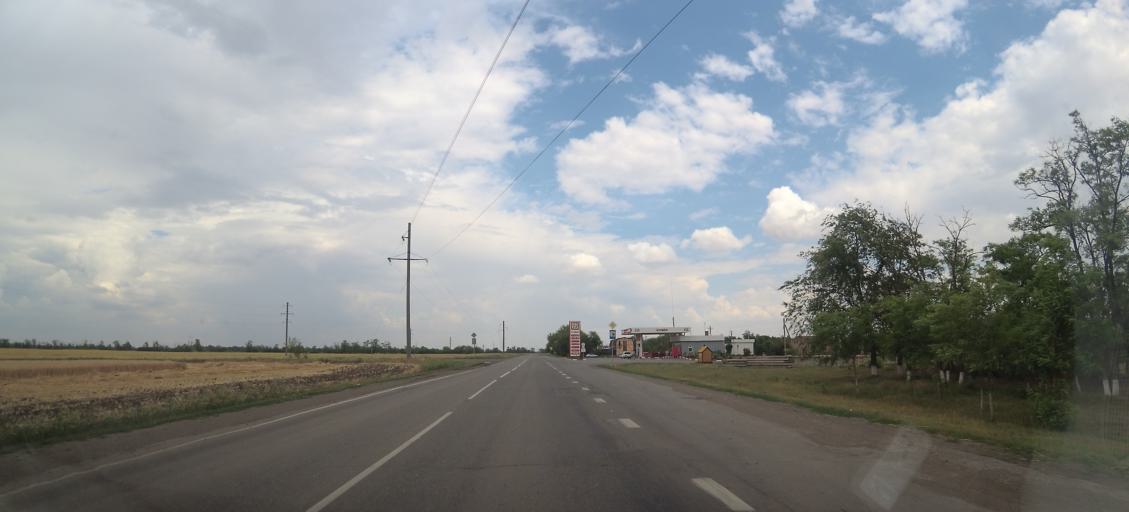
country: RU
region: Rostov
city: Peschanokopskoye
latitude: 46.2493
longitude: 41.2897
